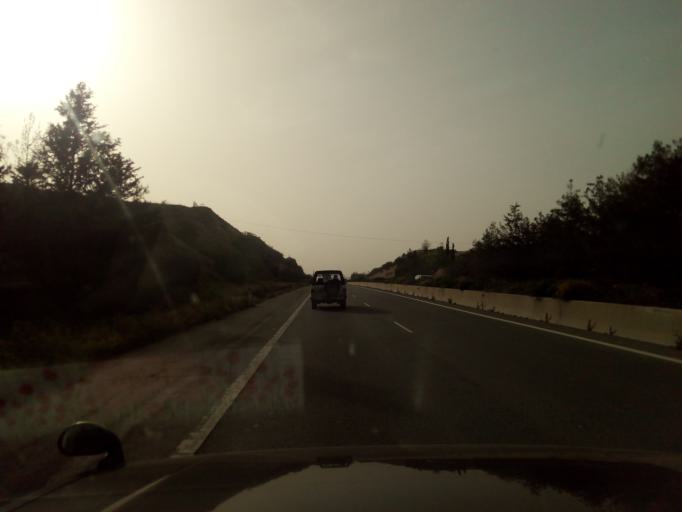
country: CY
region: Lefkosia
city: Dali
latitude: 34.9981
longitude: 33.4262
